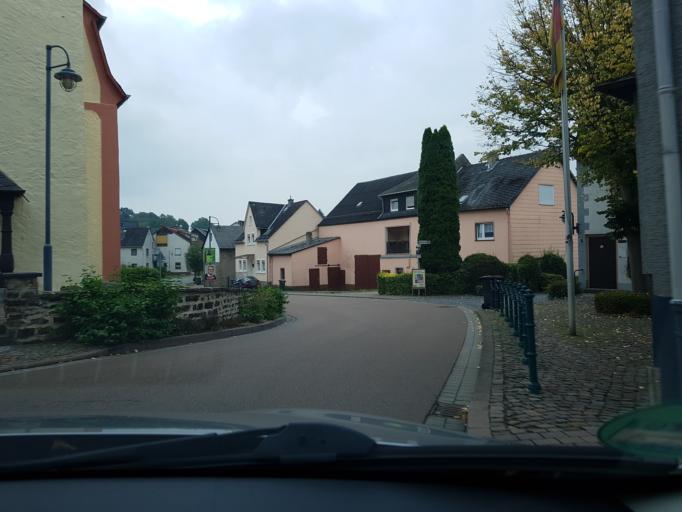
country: DE
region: Rheinland-Pfalz
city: Becheln
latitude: 50.2930
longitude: 7.7185
